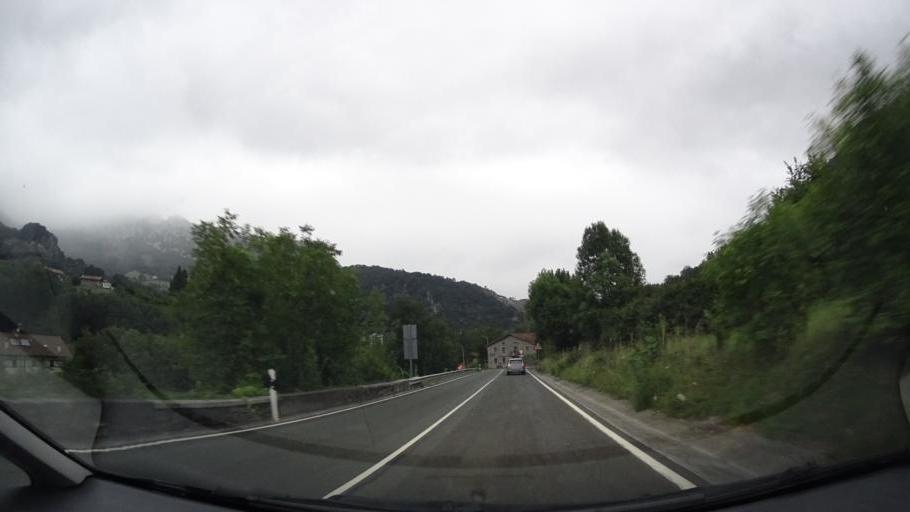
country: ES
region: Basque Country
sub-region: Bizkaia
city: Manaria
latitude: 43.1333
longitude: -2.6629
